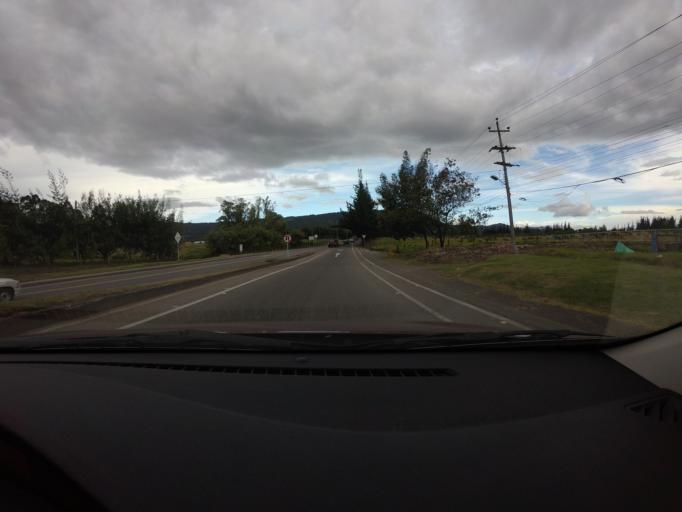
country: CO
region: Cundinamarca
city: Sopo
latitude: 4.9394
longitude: -73.9599
